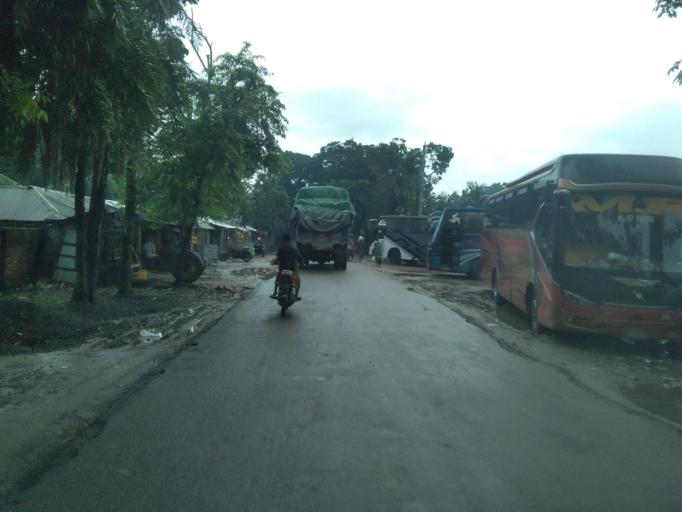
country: IN
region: West Bengal
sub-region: North 24 Parganas
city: Taki
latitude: 22.3484
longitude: 89.1036
